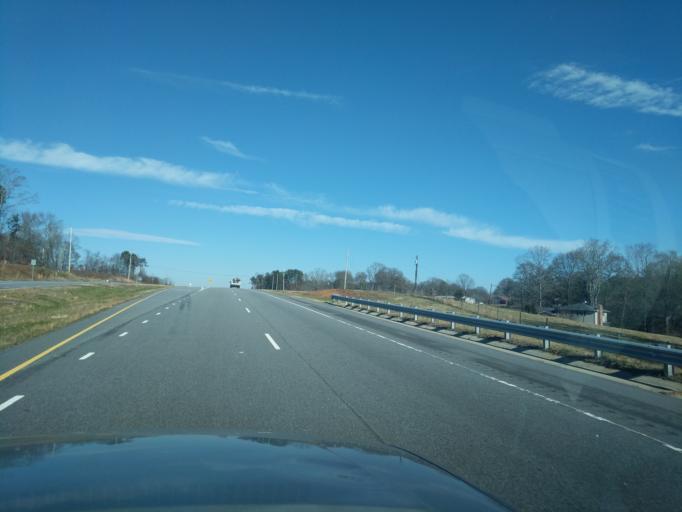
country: US
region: South Carolina
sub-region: Spartanburg County
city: Mayo
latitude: 35.1938
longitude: -81.8406
